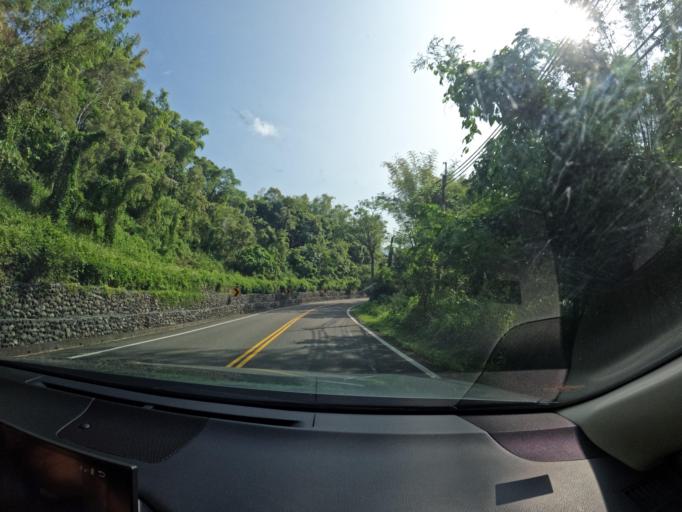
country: TW
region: Taiwan
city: Yujing
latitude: 23.0615
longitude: 120.5611
